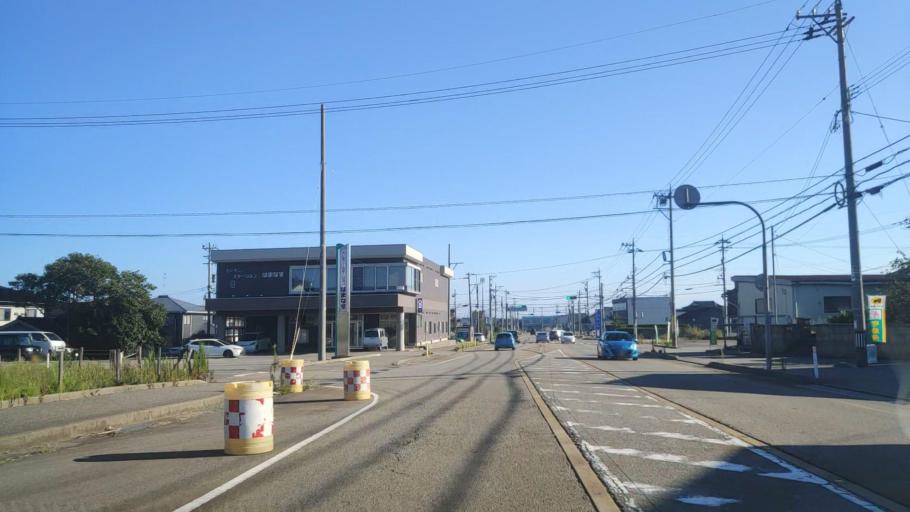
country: JP
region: Ishikawa
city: Tsubata
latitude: 36.7411
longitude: 136.7064
